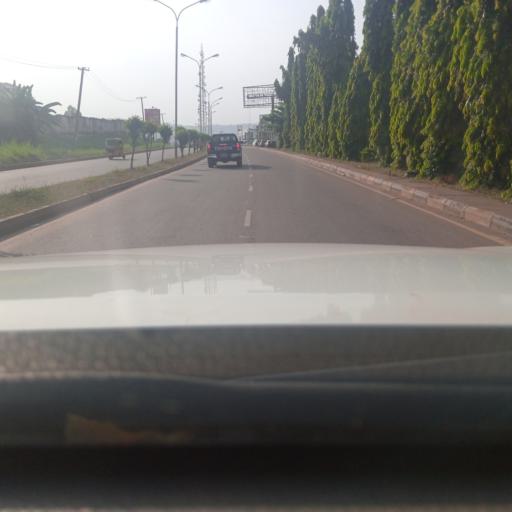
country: NG
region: Enugu
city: Enugu
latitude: 6.4409
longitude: 7.5122
